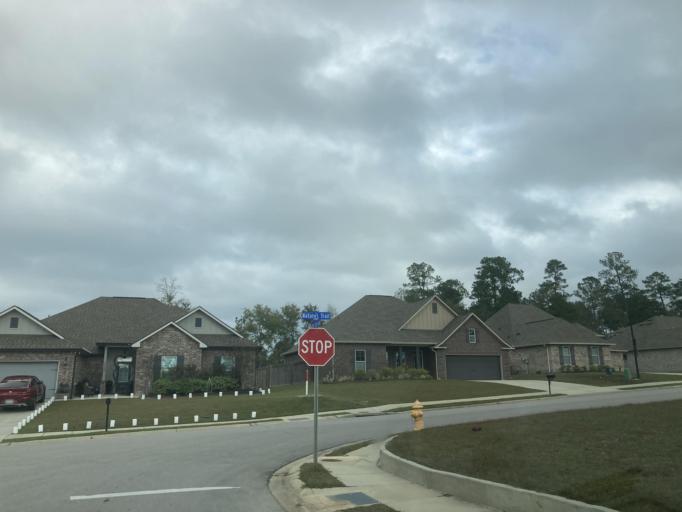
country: US
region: Mississippi
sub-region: Harrison County
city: D'Iberville
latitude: 30.4782
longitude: -88.9938
